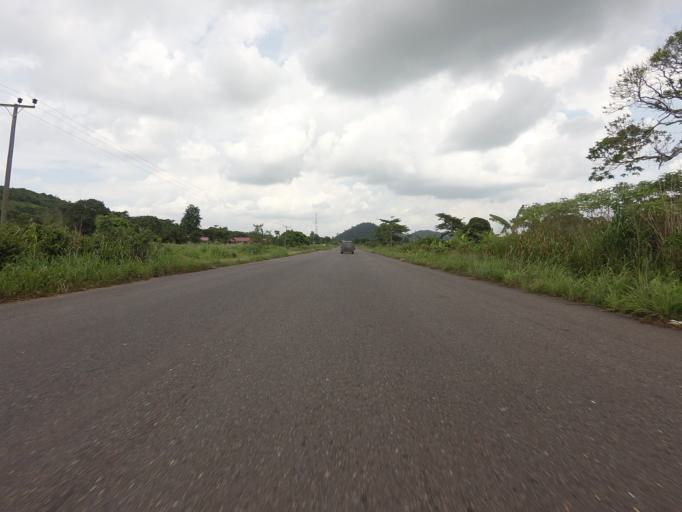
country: GH
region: Volta
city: Ho
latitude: 6.4362
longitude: 0.1711
